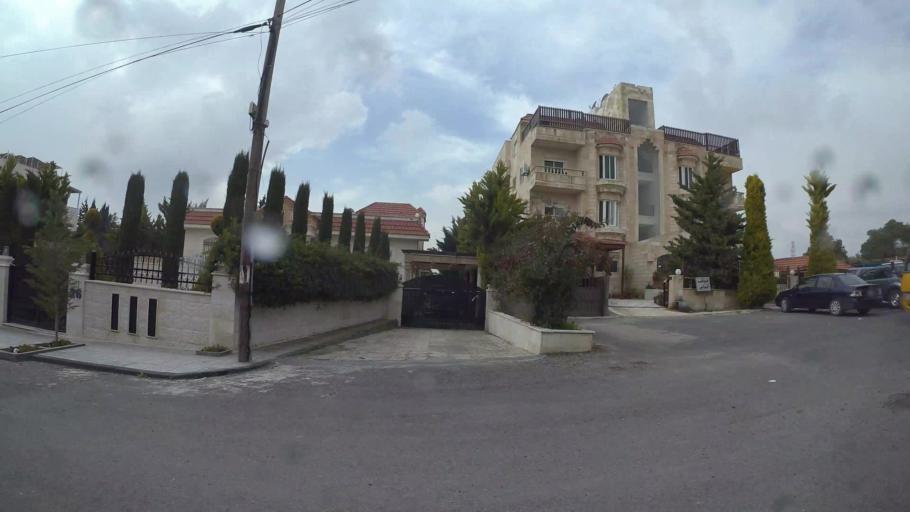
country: JO
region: Amman
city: Umm as Summaq
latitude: 31.8932
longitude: 35.8599
